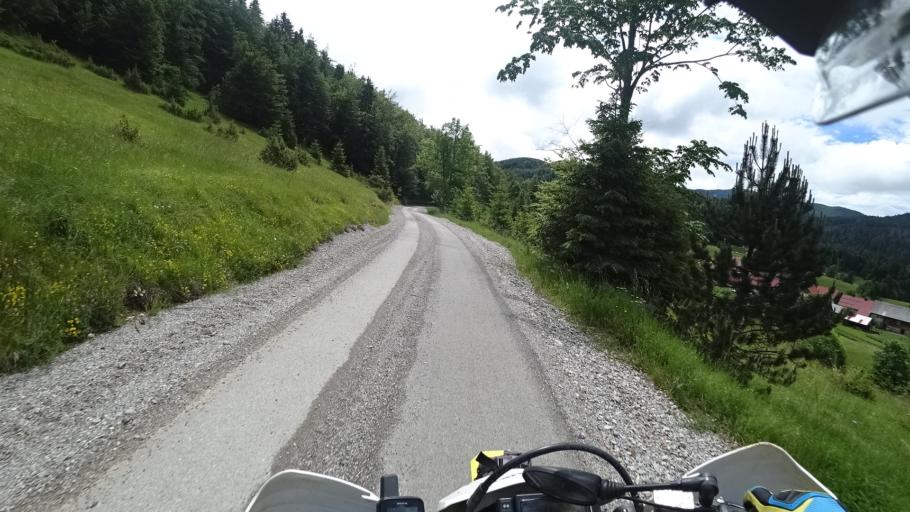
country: HR
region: Primorsko-Goranska
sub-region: Grad Delnice
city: Delnice
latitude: 45.3265
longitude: 14.7920
